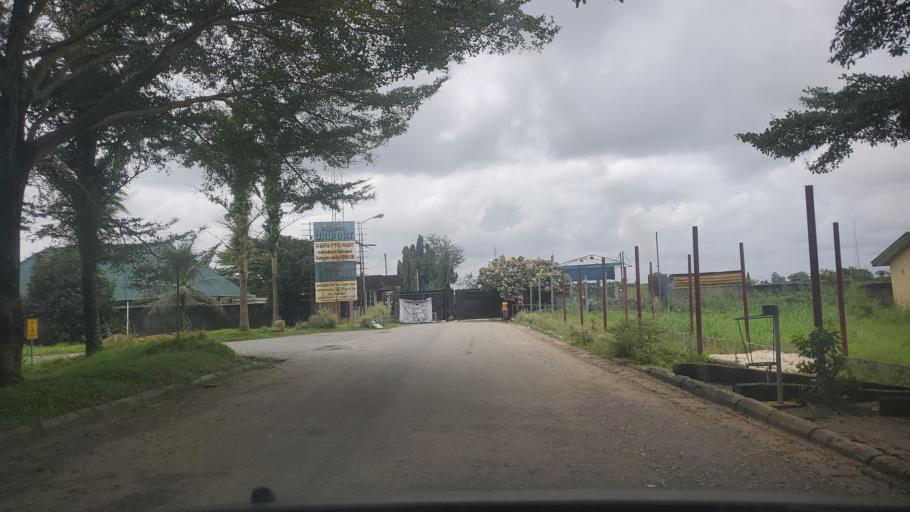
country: NG
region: Rivers
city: Emuoha
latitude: 4.9002
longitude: 6.9248
